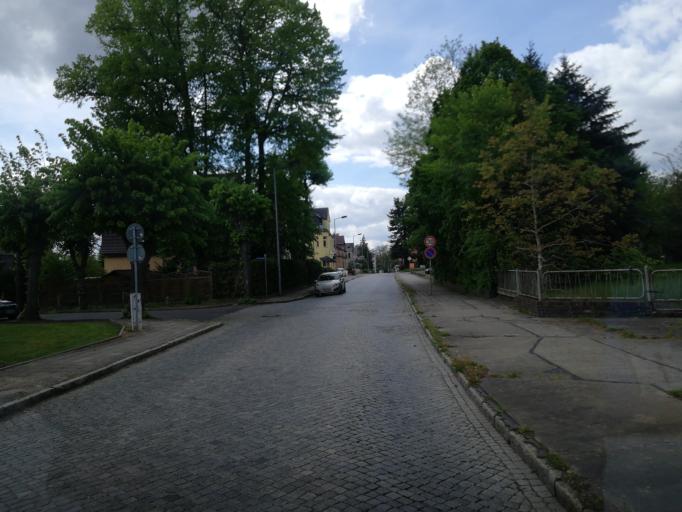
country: DE
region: Brandenburg
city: Lauchhammer
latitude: 51.5003
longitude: 13.7965
